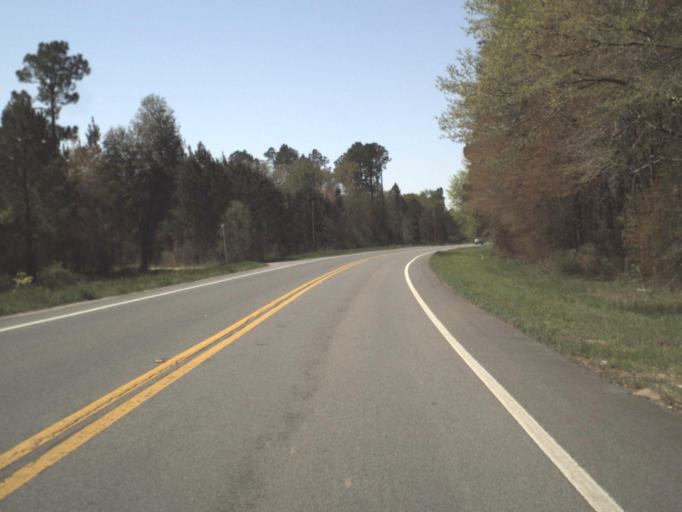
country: US
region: Florida
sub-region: Jackson County
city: Graceville
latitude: 30.9111
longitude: -85.4327
